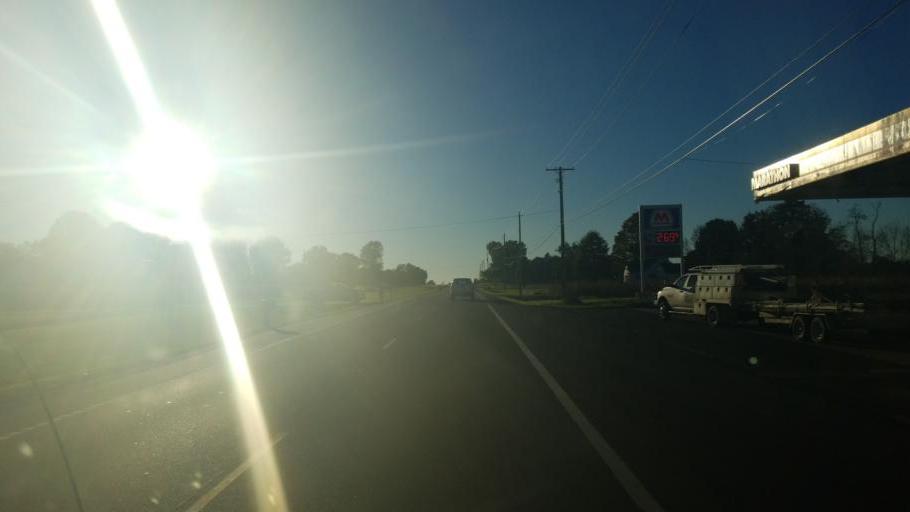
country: US
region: Ohio
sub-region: Mahoning County
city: Sebring
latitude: 40.9016
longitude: -81.0068
